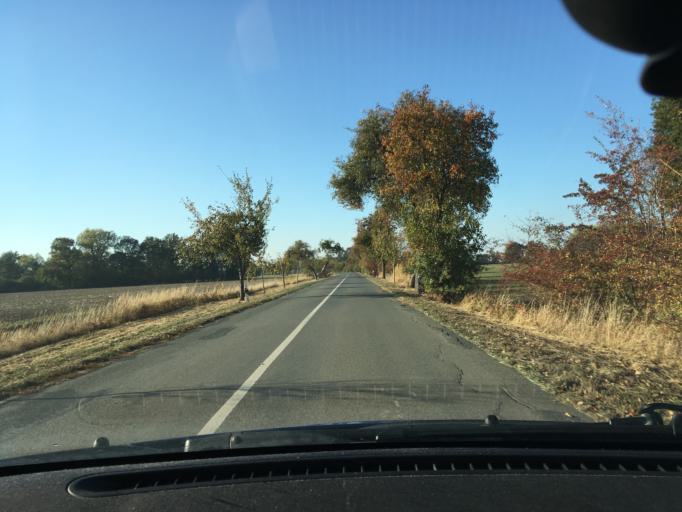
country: DE
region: Lower Saxony
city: Hitzacker
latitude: 53.1503
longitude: 11.0932
